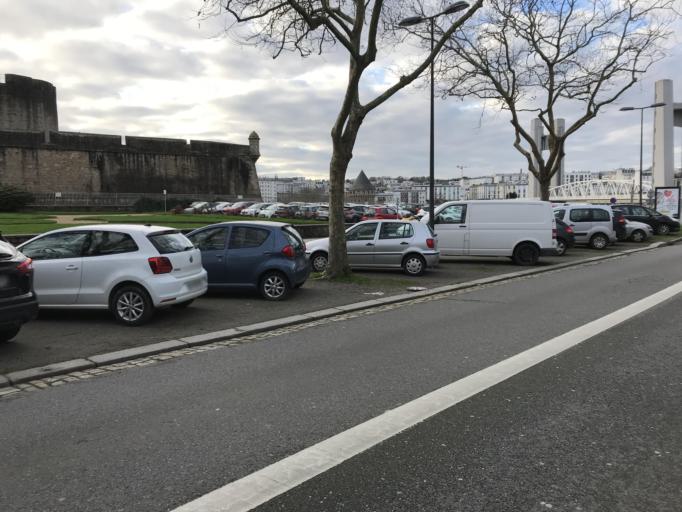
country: FR
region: Brittany
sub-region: Departement du Finistere
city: Brest
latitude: 48.3831
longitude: -4.4927
